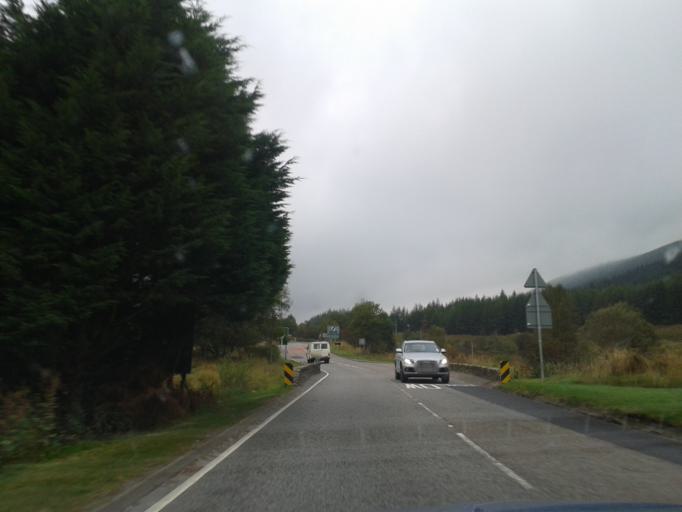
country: GB
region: Scotland
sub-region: Argyll and Bute
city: Garelochhead
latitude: 56.4383
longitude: -4.7139
